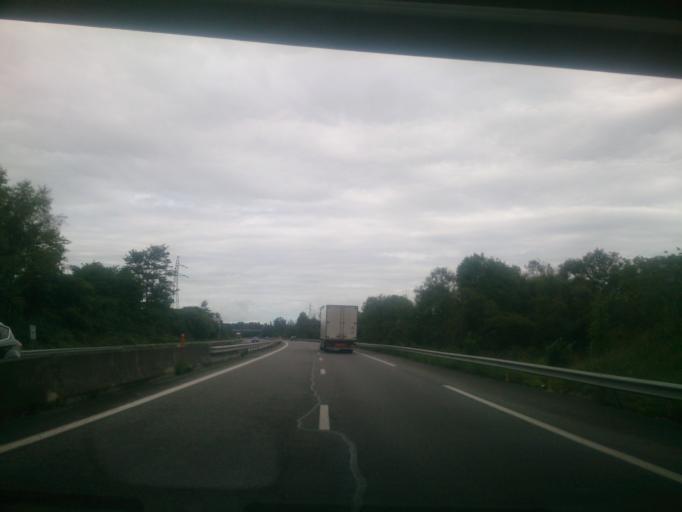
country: FR
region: Midi-Pyrenees
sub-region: Departement des Hautes-Pyrenees
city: Lannemezan
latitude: 43.1074
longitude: 0.4644
